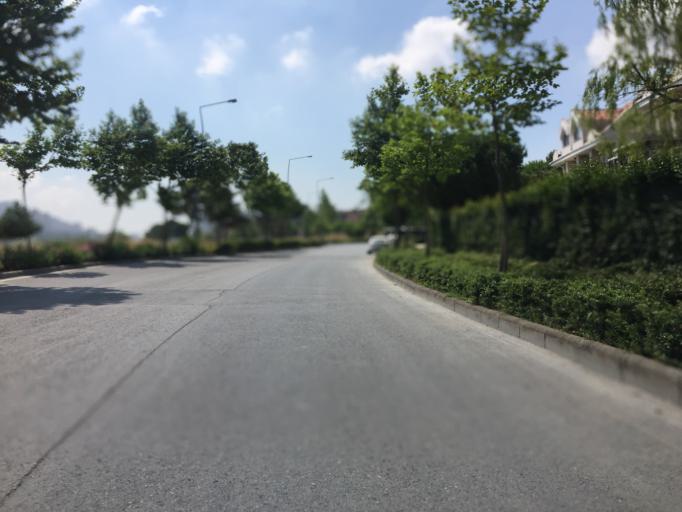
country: TR
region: Istanbul
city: Esenyurt
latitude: 41.0871
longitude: 28.6711
